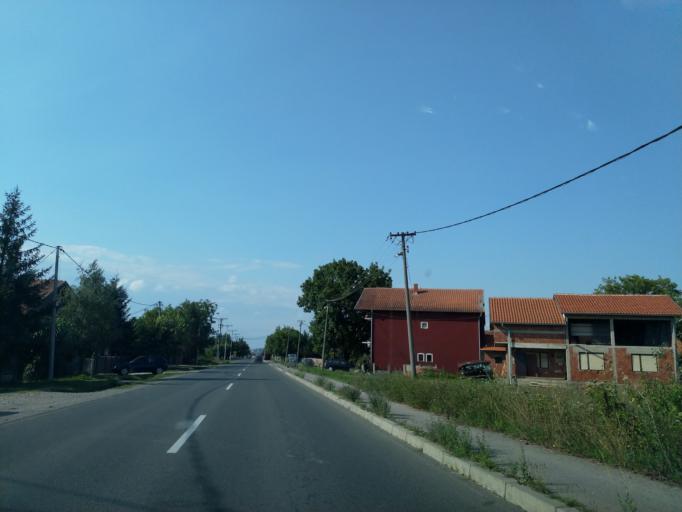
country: RS
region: Central Serbia
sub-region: Pomoravski Okrug
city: Paracin
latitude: 43.8283
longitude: 21.4173
